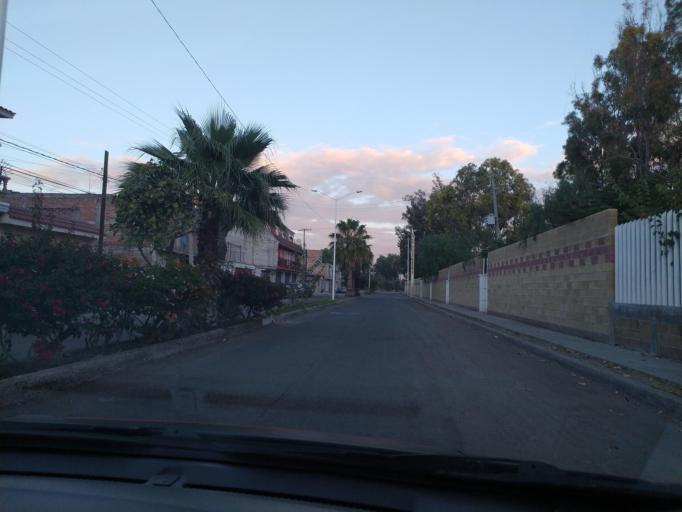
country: MX
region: Guanajuato
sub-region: San Francisco del Rincon
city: Fraccionamiento la Mezquitera
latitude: 21.0103
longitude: -101.8401
